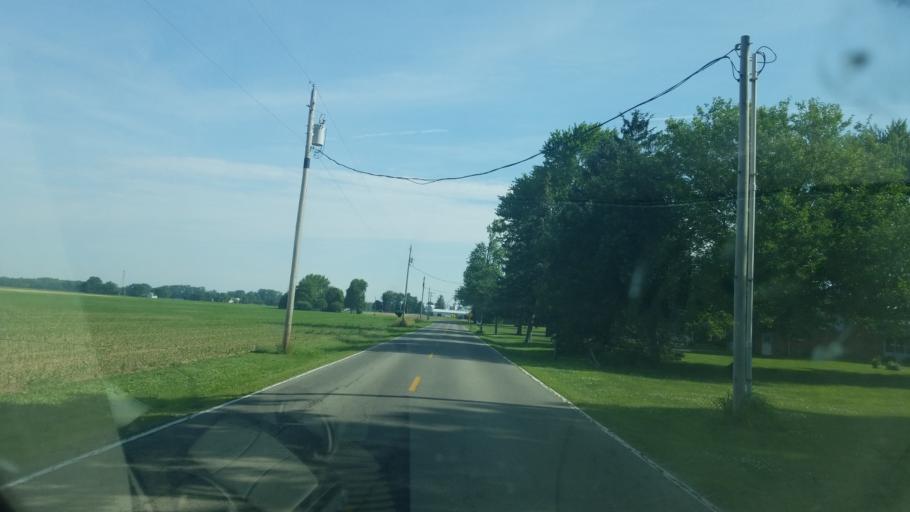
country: US
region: Ohio
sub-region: Hancock County
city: Findlay
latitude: 41.0198
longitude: -83.5881
